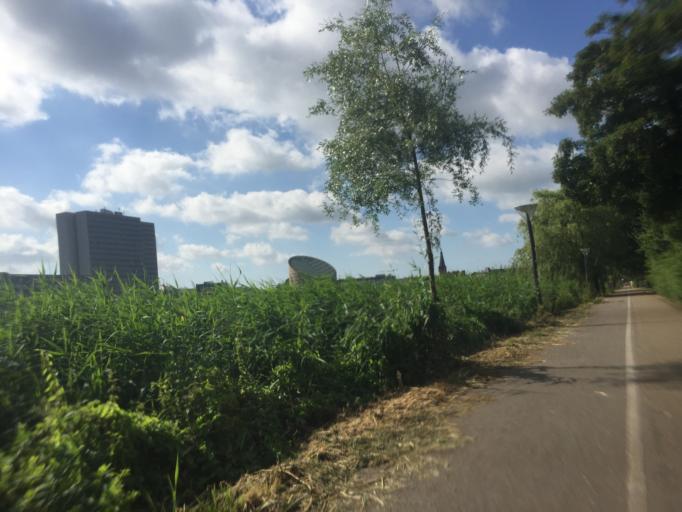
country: DK
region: Capital Region
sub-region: Kobenhavn
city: Copenhagen
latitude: 55.6774
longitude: 12.5563
